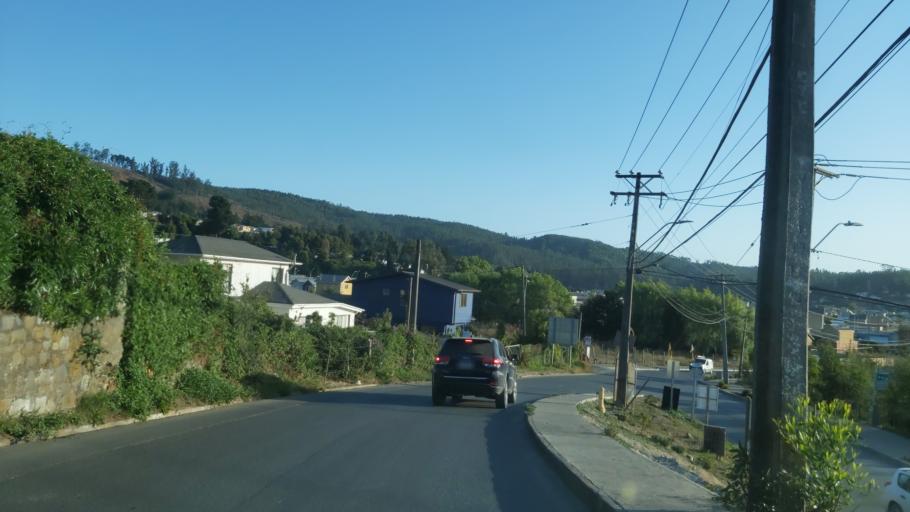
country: CL
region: Biobio
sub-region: Provincia de Concepcion
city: Tome
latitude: -36.5432
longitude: -72.9306
